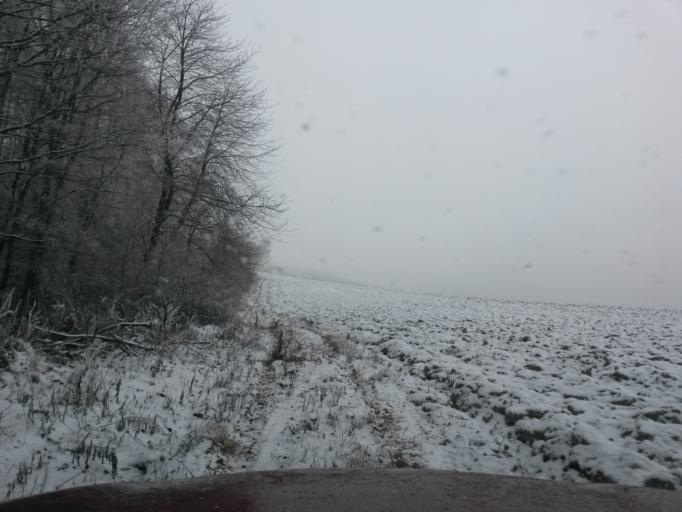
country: SK
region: Presovsky
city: Sabinov
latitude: 48.9796
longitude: 21.0872
